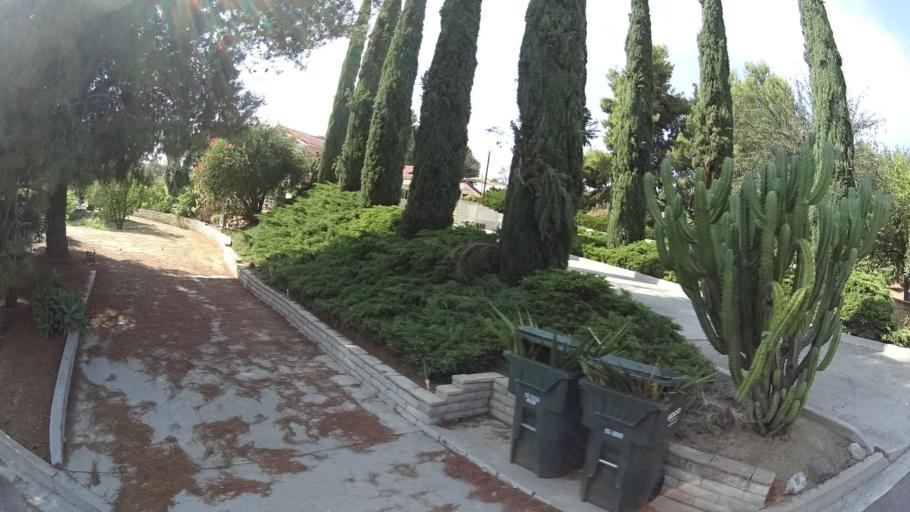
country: US
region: California
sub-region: San Diego County
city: Escondido
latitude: 33.0879
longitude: -117.0610
